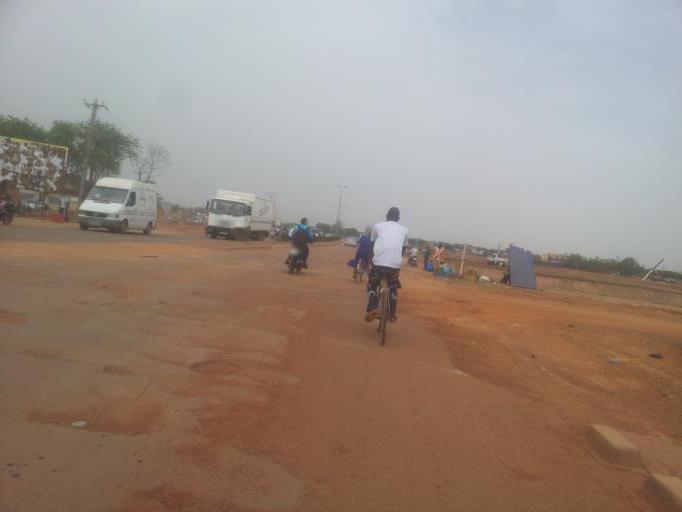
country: BF
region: Centre
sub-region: Kadiogo Province
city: Ouagadougou
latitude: 12.3857
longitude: -1.5581
